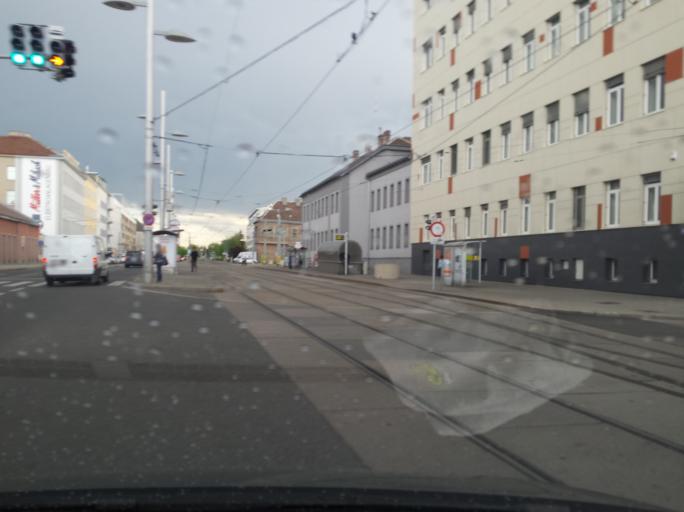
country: AT
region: Lower Austria
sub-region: Politischer Bezirk Wien-Umgebung
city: Schwechat
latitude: 48.1675
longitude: 16.4233
